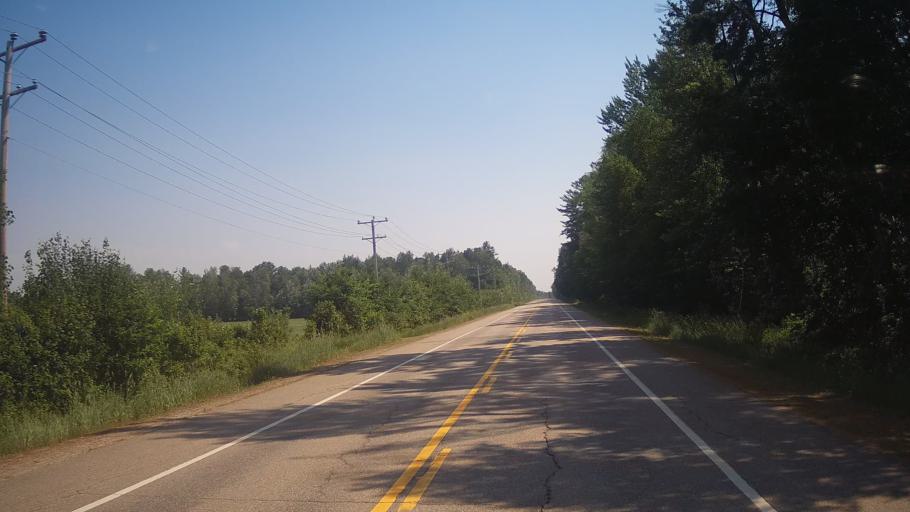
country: CA
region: Ontario
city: Pembroke
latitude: 45.8448
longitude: -77.0135
